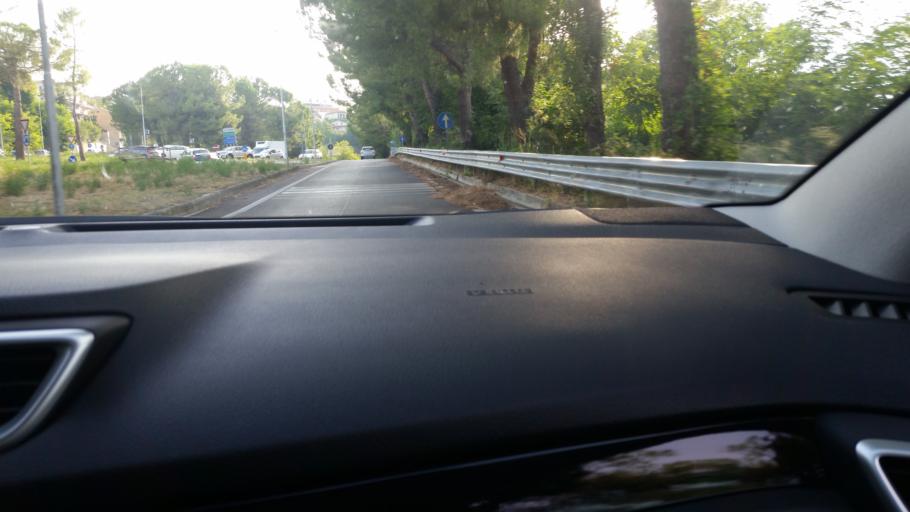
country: IT
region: Abruzzo
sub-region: Provincia di Chieti
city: Torrevecchia
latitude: 42.3528
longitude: 14.1813
